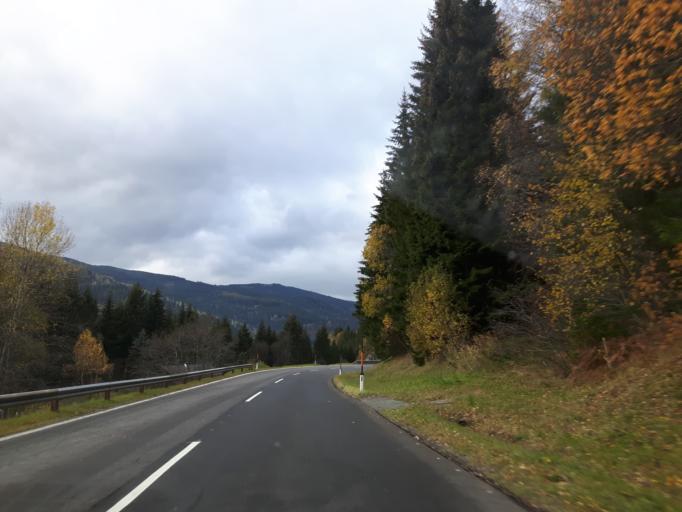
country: AT
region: Styria
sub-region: Politischer Bezirk Deutschlandsberg
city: Soboth
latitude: 46.7047
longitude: 15.1054
